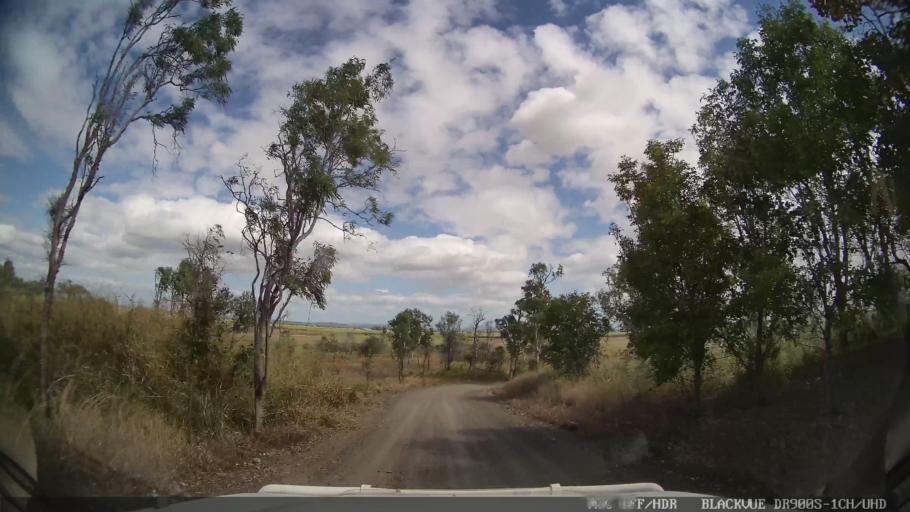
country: AU
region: Queensland
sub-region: Burdekin
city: Home Hill
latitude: -19.7094
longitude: 147.4634
